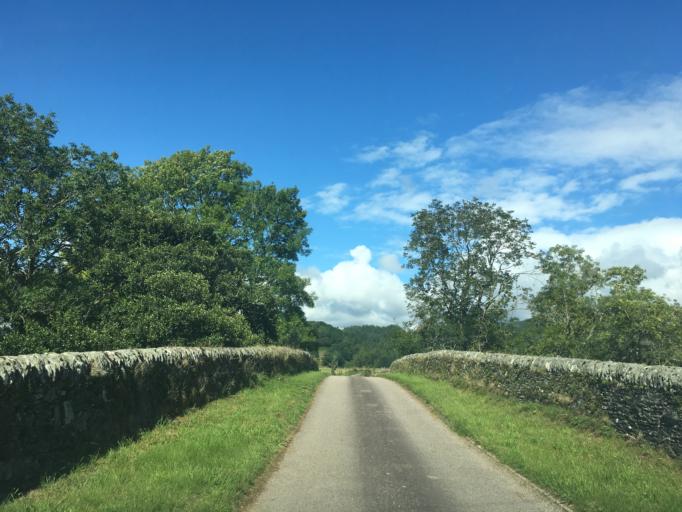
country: GB
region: Scotland
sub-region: Argyll and Bute
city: Lochgilphead
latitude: 56.0852
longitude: -5.4750
